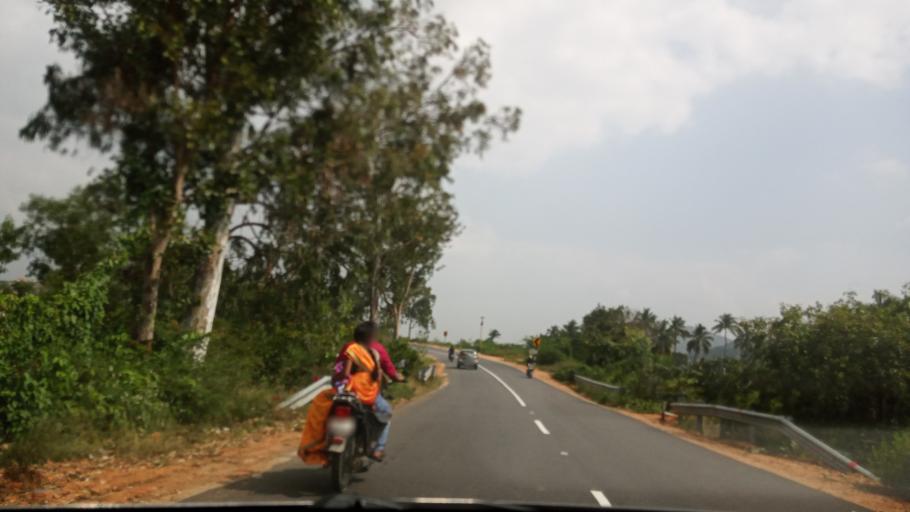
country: IN
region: Andhra Pradesh
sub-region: Chittoor
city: Madanapalle
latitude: 13.6352
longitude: 78.6066
